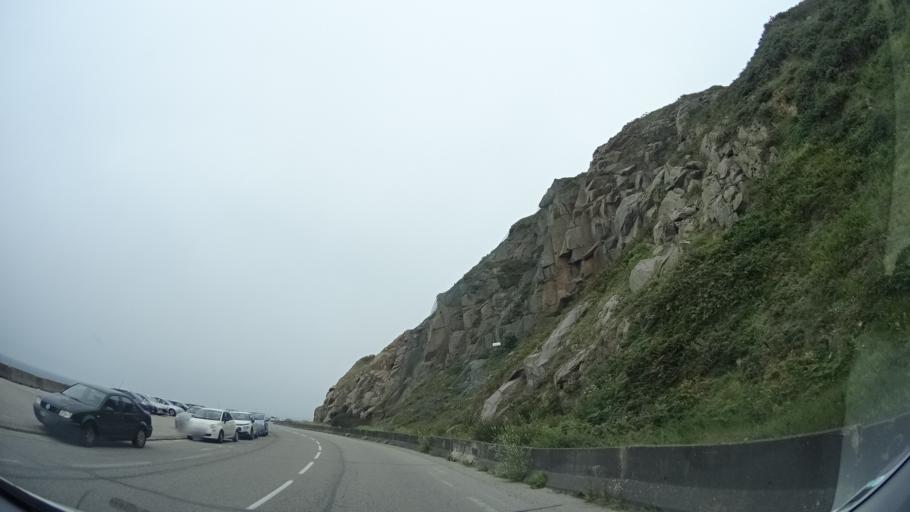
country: FR
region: Lower Normandy
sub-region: Departement de la Manche
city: Flamanville
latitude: 49.5471
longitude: -1.8696
